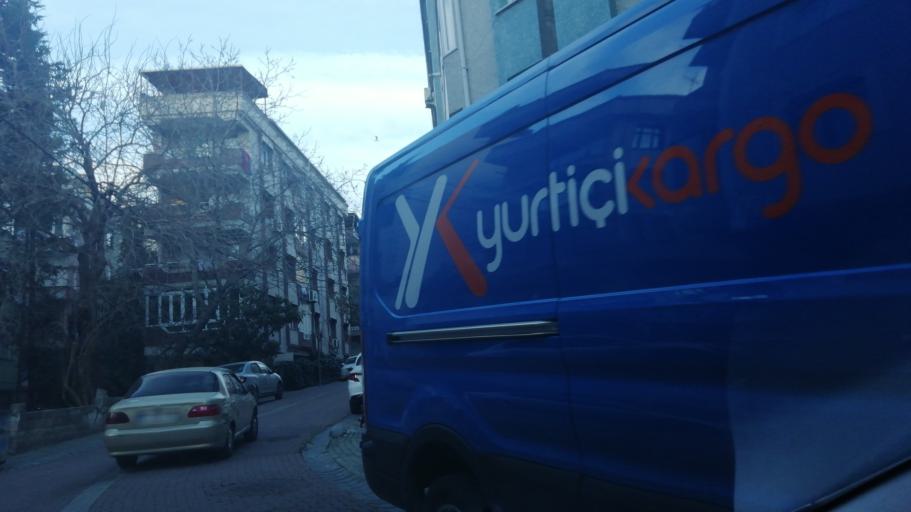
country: TR
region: Istanbul
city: Yakuplu
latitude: 40.9748
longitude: 28.7325
